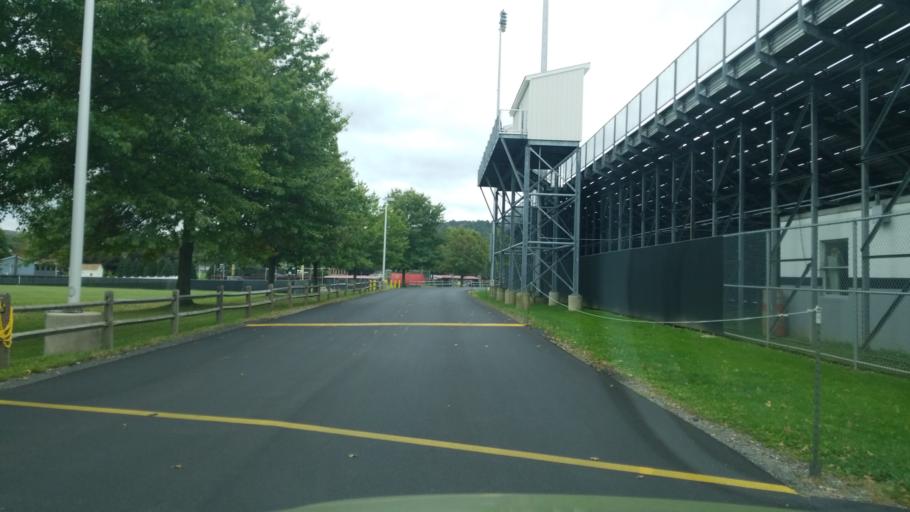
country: US
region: Pennsylvania
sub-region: Clearfield County
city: Hyde
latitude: 40.9923
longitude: -78.4807
